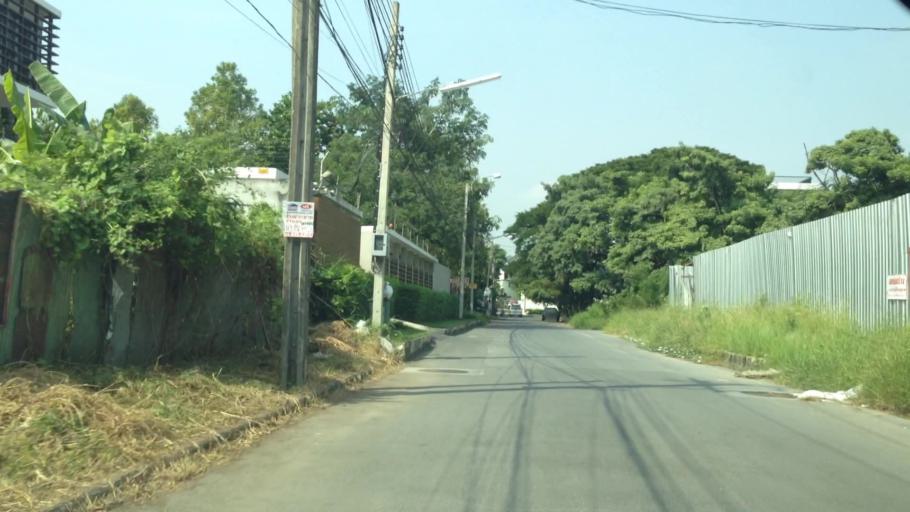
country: TH
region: Bangkok
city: Bang Na
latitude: 13.6841
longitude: 100.6569
